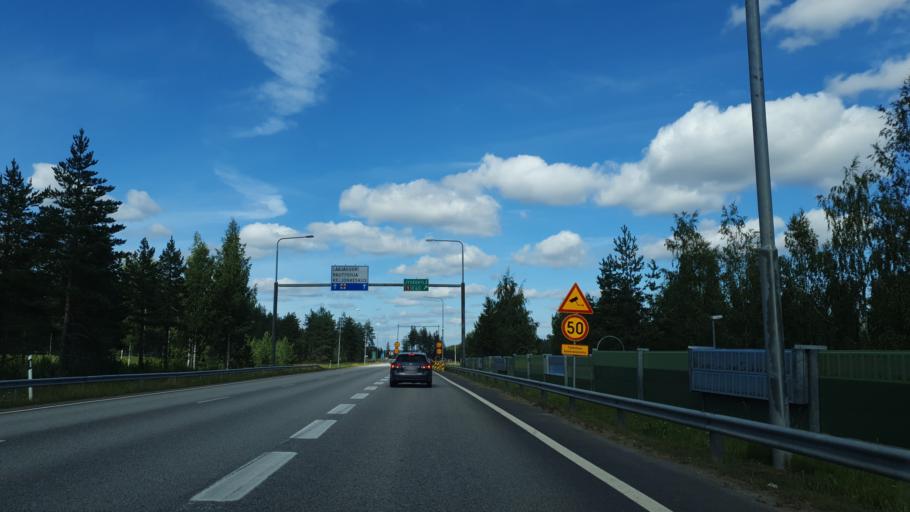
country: FI
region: Central Finland
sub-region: Jyvaeskylae
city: Jyvaeskylae
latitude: 62.2071
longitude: 25.7129
